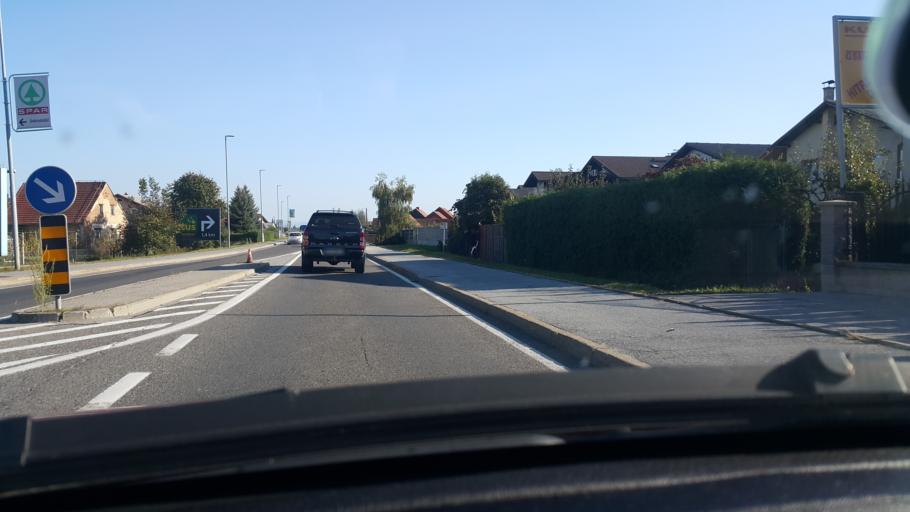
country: SI
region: Miklavz na Dravskem Polju
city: Miklavz na Dravskem Polju
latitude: 46.5102
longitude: 15.6928
